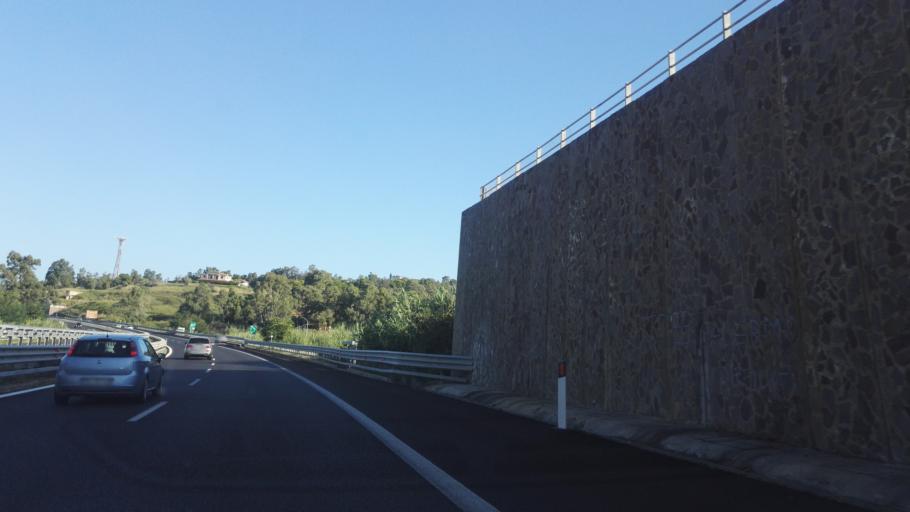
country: IT
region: Calabria
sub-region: Provincia di Catanzaro
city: Falerna Scalo
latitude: 38.9729
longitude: 16.1524
